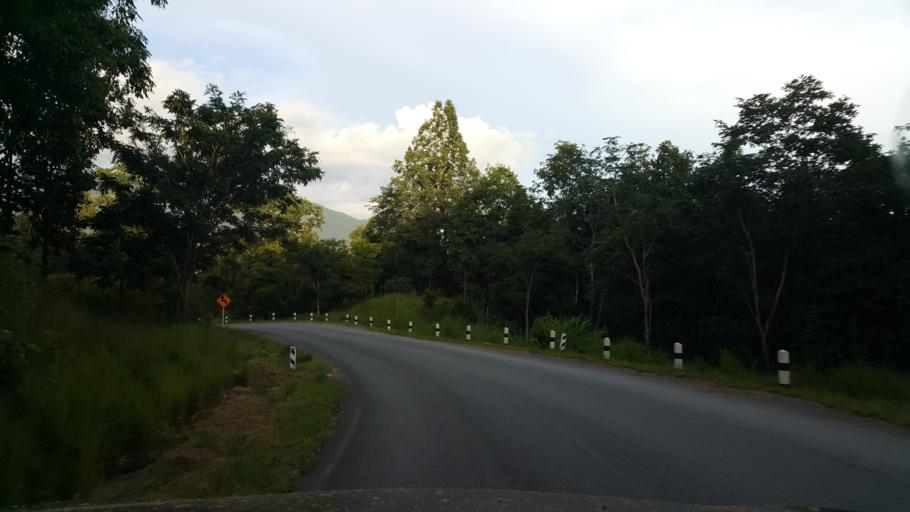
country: TH
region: Mae Hong Son
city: Mae Hi
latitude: 19.1887
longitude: 98.4177
